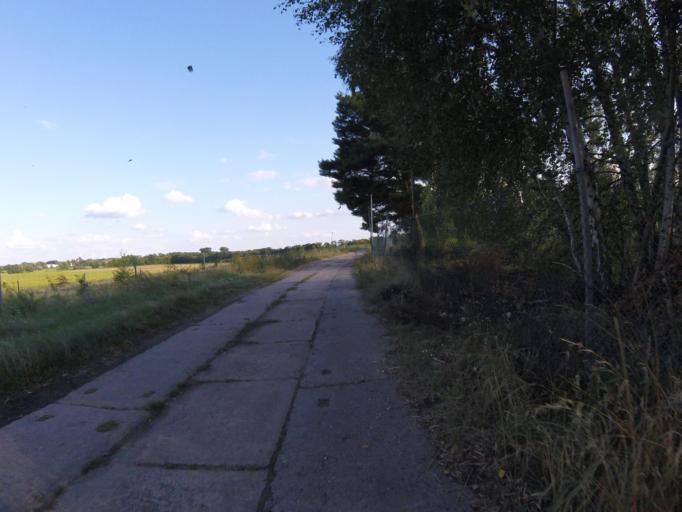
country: DE
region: Brandenburg
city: Mittenwalde
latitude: 52.2779
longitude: 13.5153
